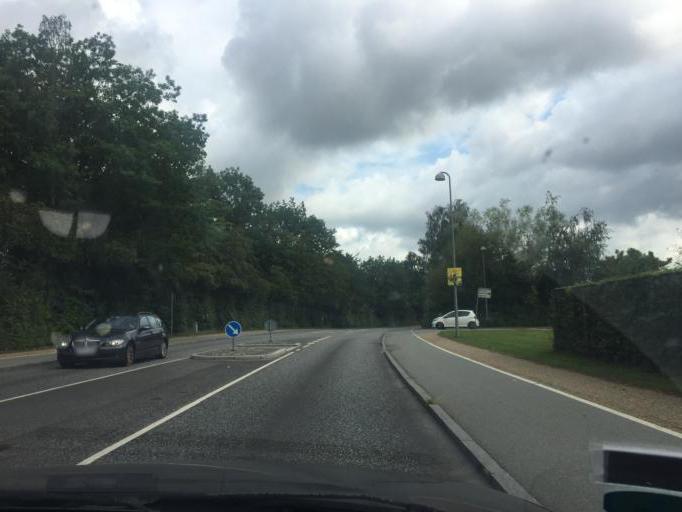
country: DK
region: Capital Region
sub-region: Allerod Kommune
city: Lillerod
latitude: 55.8836
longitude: 12.3520
